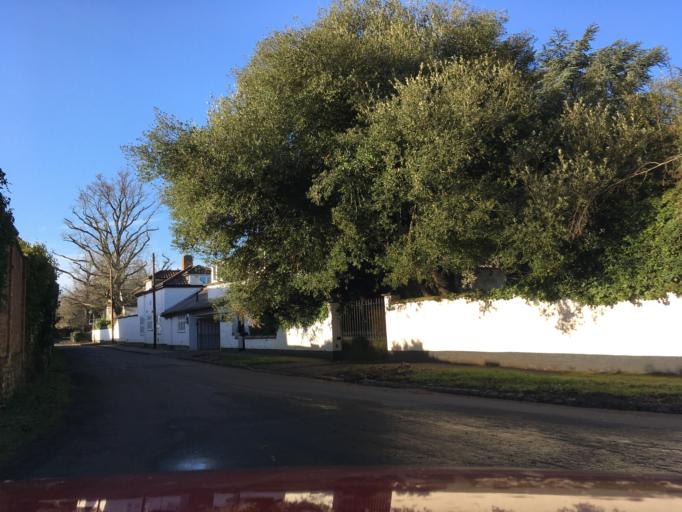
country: GB
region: England
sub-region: Warwickshire
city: Stratford-upon-Avon
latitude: 52.2063
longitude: -1.6583
